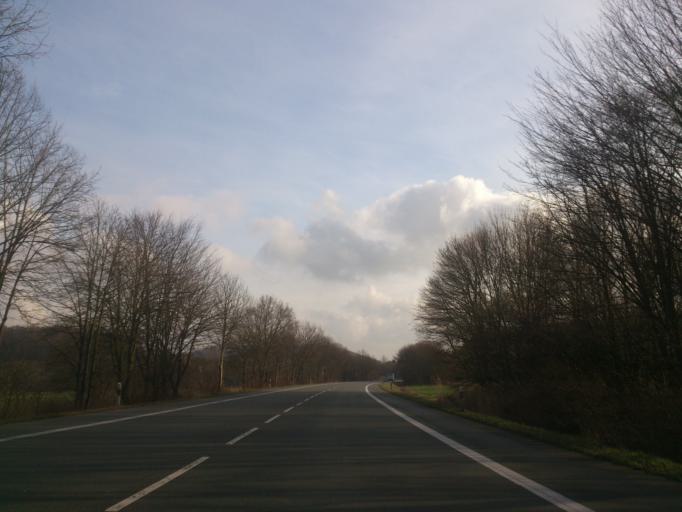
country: DE
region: North Rhine-Westphalia
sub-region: Regierungsbezirk Detmold
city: Bad Driburg
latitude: 51.7230
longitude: 9.0559
